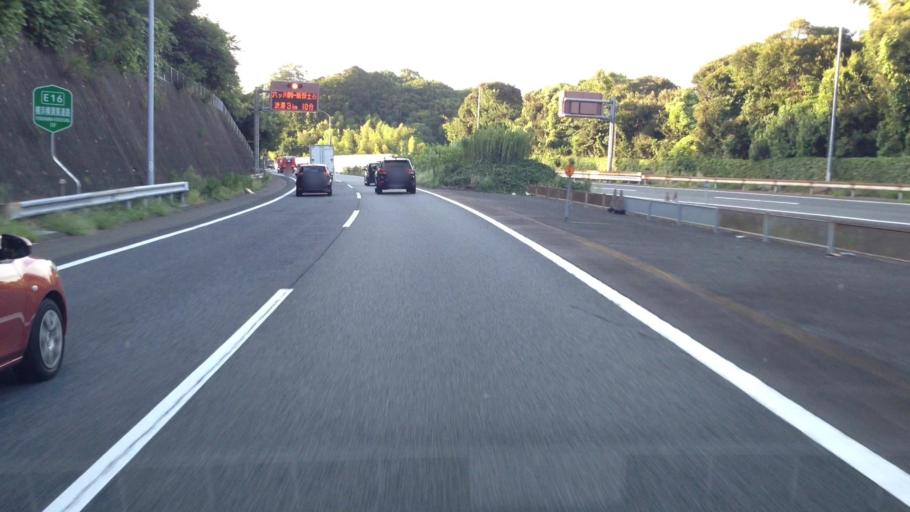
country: JP
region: Kanagawa
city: Kamakura
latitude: 35.3636
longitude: 139.5984
